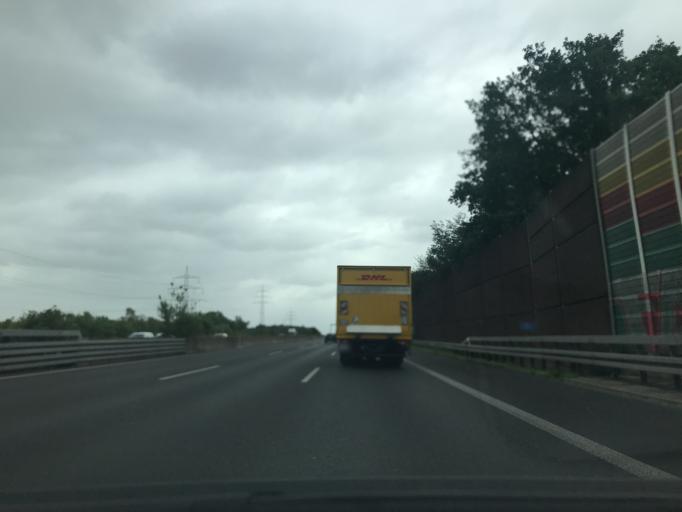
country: DE
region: North Rhine-Westphalia
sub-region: Regierungsbezirk Dusseldorf
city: Dusseldorf
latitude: 51.1605
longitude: 6.7459
